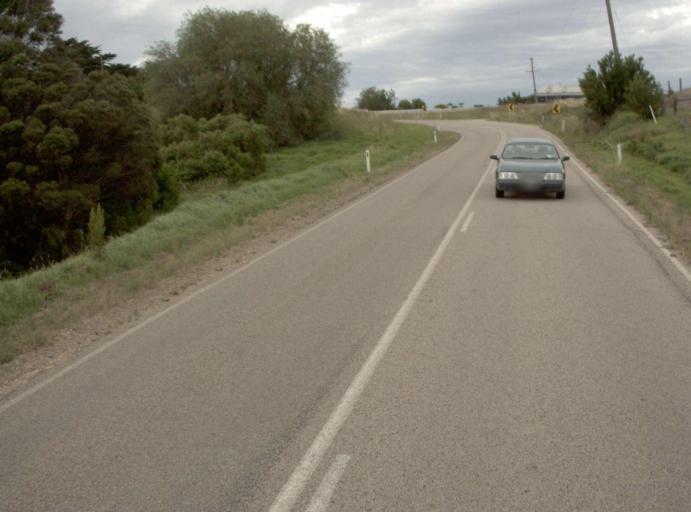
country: AU
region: Victoria
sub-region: East Gippsland
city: Bairnsdale
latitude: -37.8049
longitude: 147.4767
